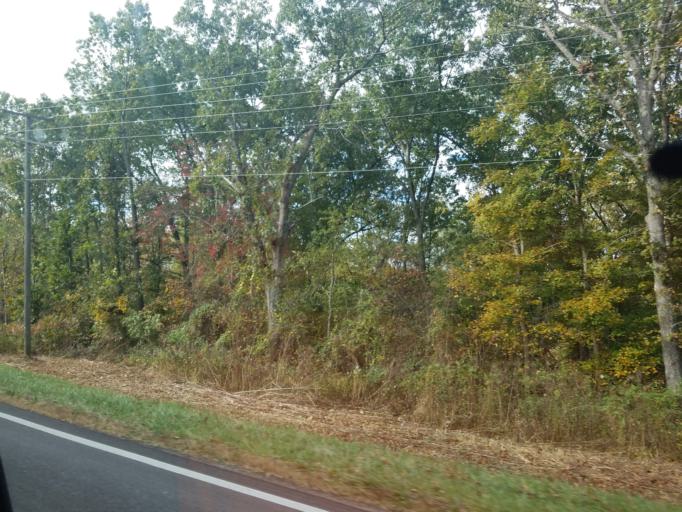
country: US
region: Ohio
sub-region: Vinton County
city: McArthur
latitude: 39.1836
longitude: -82.4652
